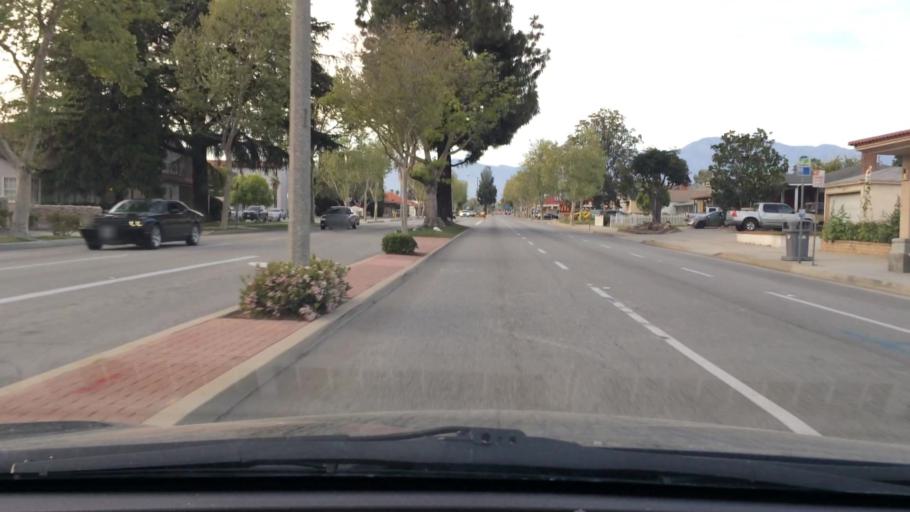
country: US
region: California
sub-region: San Bernardino County
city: Chino
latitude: 34.0224
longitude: -117.6894
